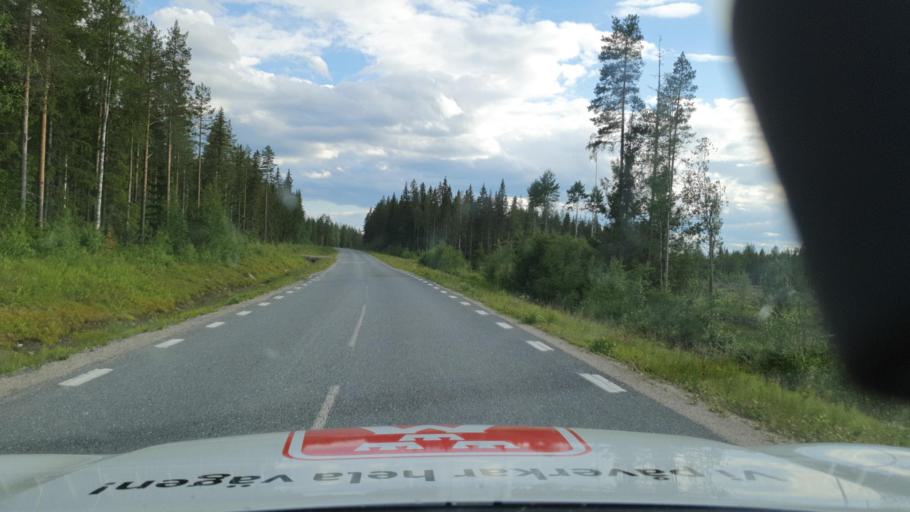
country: SE
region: Vaesterbotten
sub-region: Vindelns Kommun
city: Vindeln
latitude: 64.4802
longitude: 19.7676
